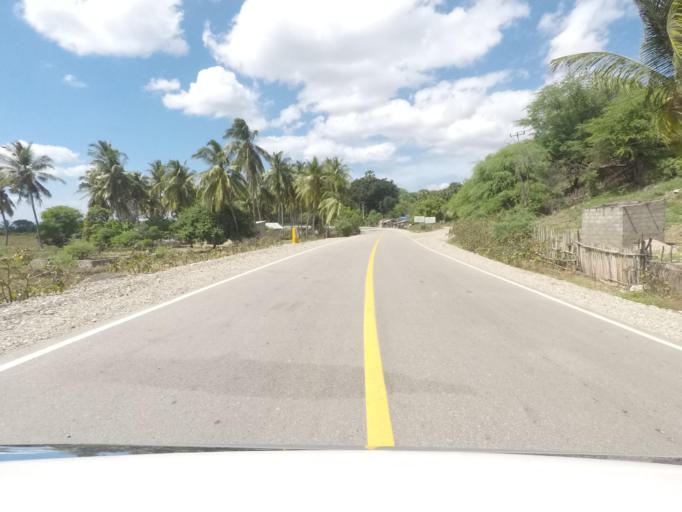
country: TL
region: Baucau
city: Baucau
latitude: -8.4079
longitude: 126.7281
